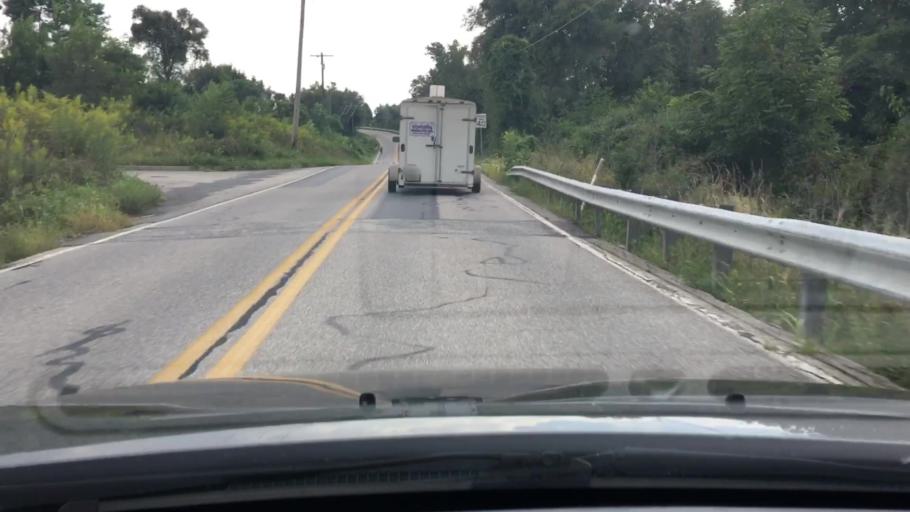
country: US
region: Pennsylvania
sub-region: Franklin County
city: Scotland
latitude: 39.9559
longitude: -77.5838
